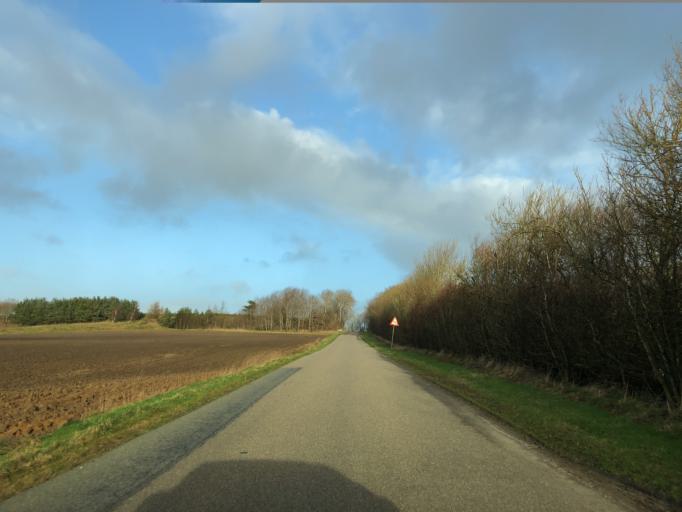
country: DK
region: Central Jutland
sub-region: Ringkobing-Skjern Kommune
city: Videbaek
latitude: 56.1871
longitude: 8.5431
